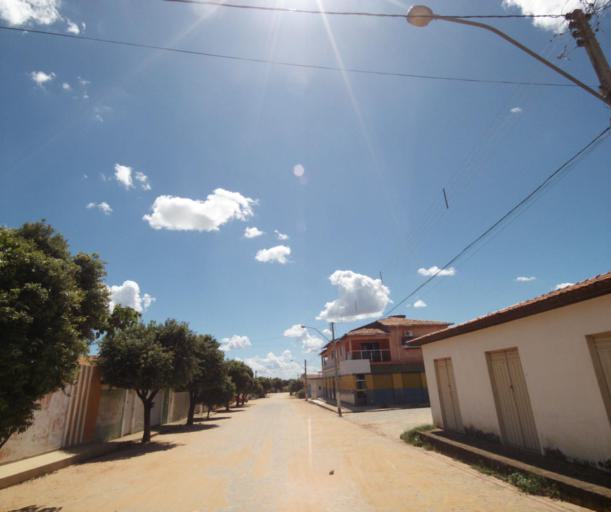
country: BR
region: Bahia
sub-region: Carinhanha
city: Carinhanha
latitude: -14.2120
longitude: -44.2805
